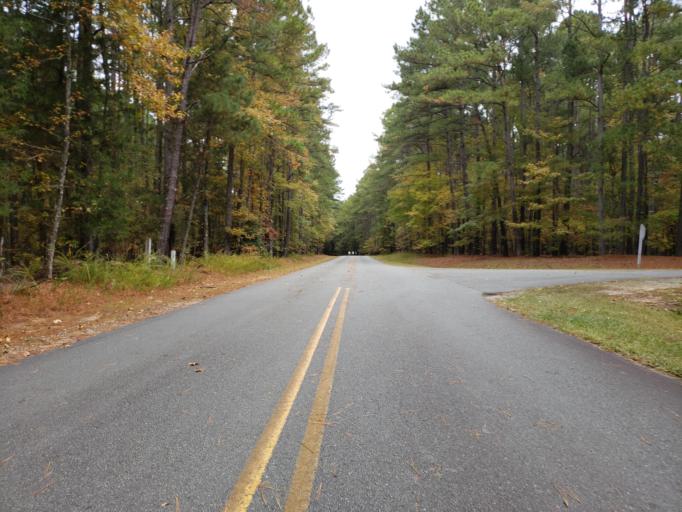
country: US
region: North Carolina
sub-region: Chatham County
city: Fearrington Village
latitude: 35.7569
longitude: -79.0442
